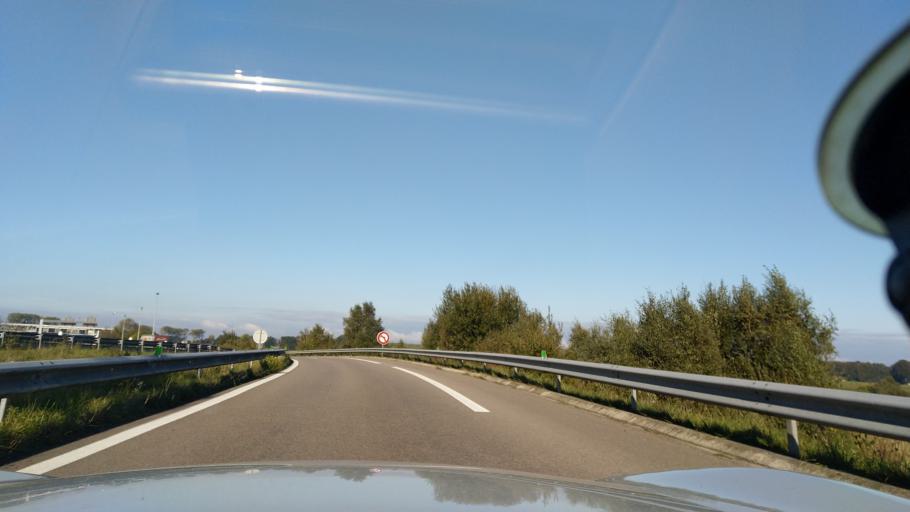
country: FR
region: Haute-Normandie
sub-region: Departement de la Seine-Maritime
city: Valliquerville
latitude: 49.6315
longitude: 0.6457
